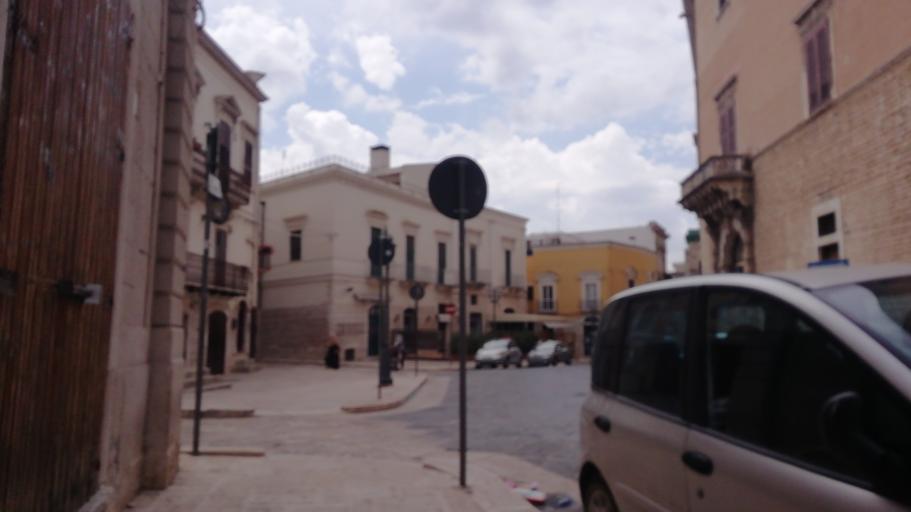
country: IT
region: Apulia
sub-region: Provincia di Barletta - Andria - Trani
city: Andria
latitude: 41.2258
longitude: 16.2969
